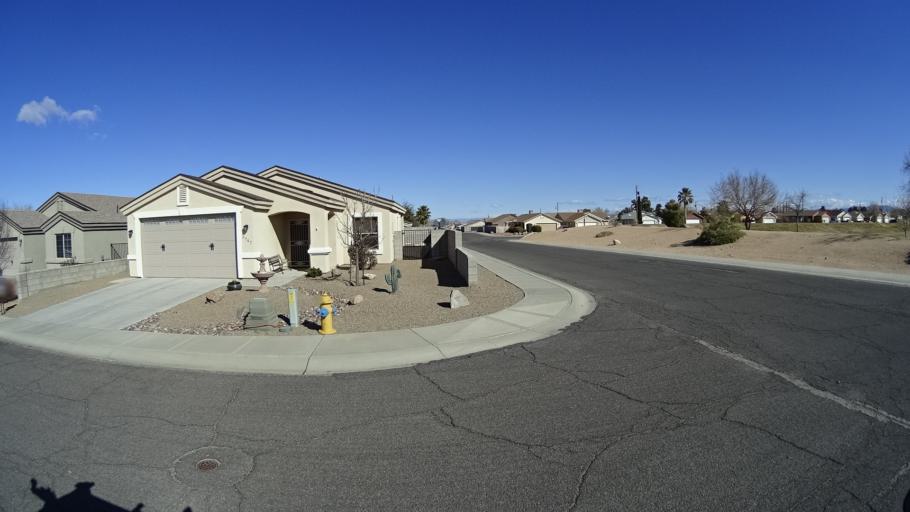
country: US
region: Arizona
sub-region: Mohave County
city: Kingman
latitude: 35.1965
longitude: -114.0138
